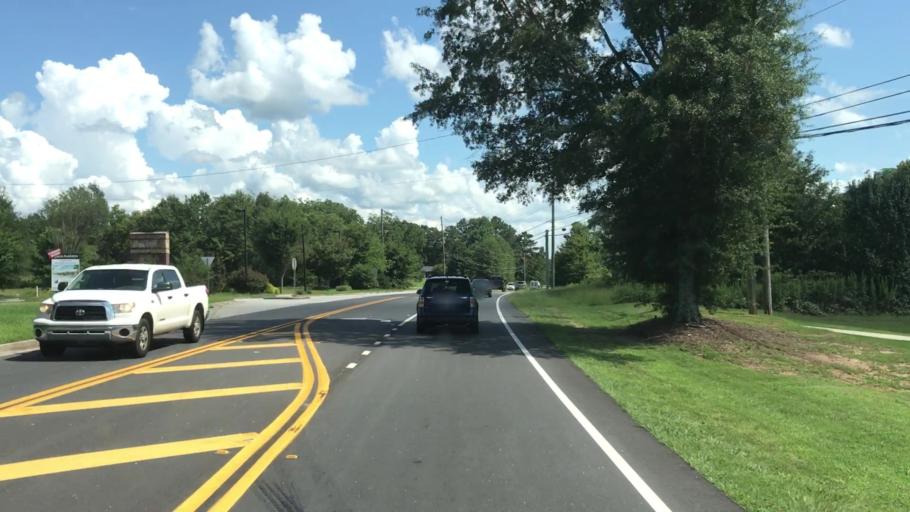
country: US
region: Georgia
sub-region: Walton County
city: Loganville
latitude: 33.8291
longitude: -83.8794
